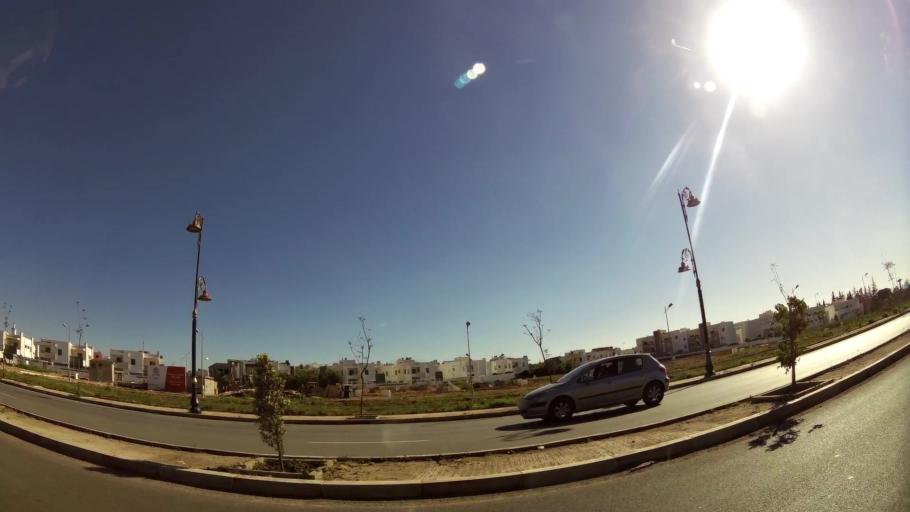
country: MA
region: Fes-Boulemane
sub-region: Fes
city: Oulad Tayeb
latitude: 33.9897
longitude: -5.0137
